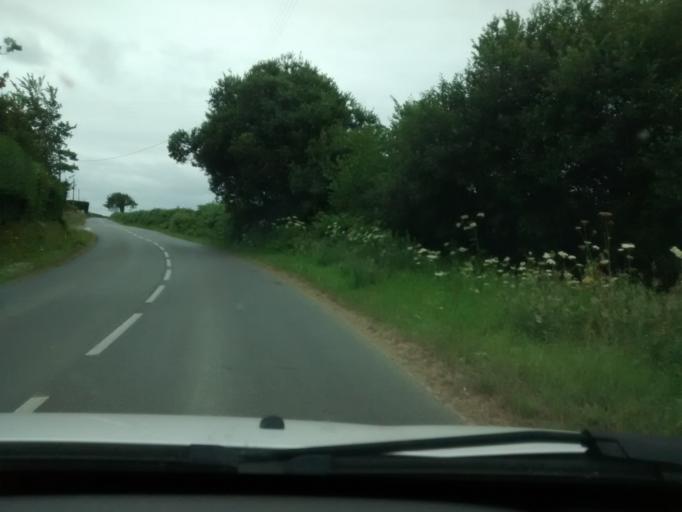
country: FR
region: Brittany
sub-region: Departement des Cotes-d'Armor
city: Penvenan
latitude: 48.8011
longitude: -3.3103
